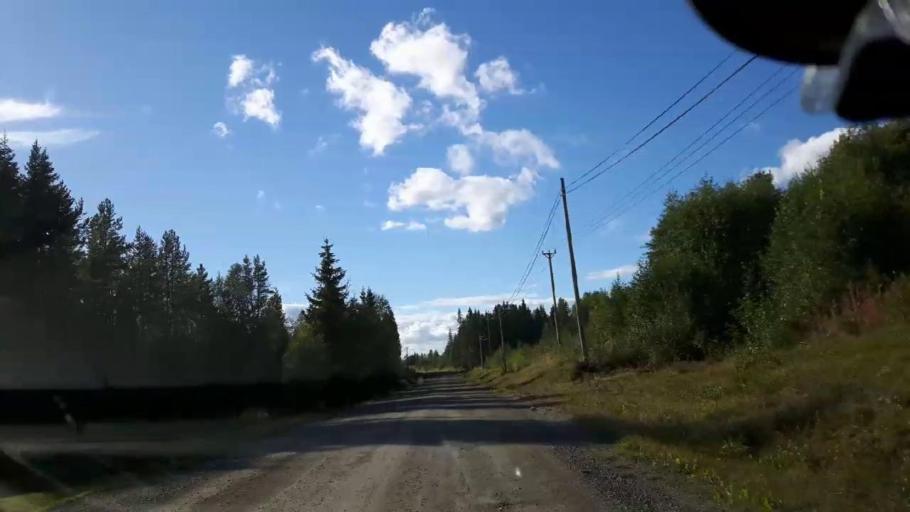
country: SE
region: Vaesternorrland
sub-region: Solleftea Kommun
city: As
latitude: 63.4645
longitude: 16.2323
